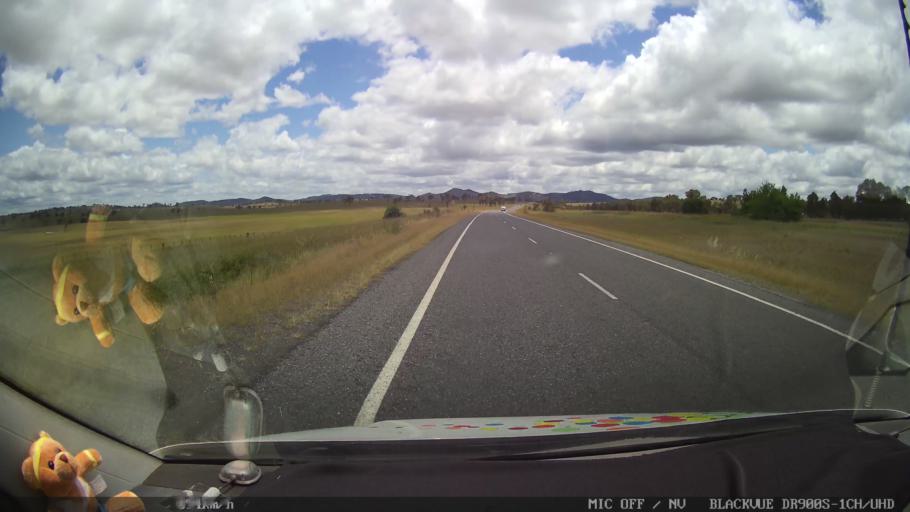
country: AU
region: New South Wales
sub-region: Glen Innes Severn
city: Glen Innes
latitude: -29.4022
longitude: 151.8730
